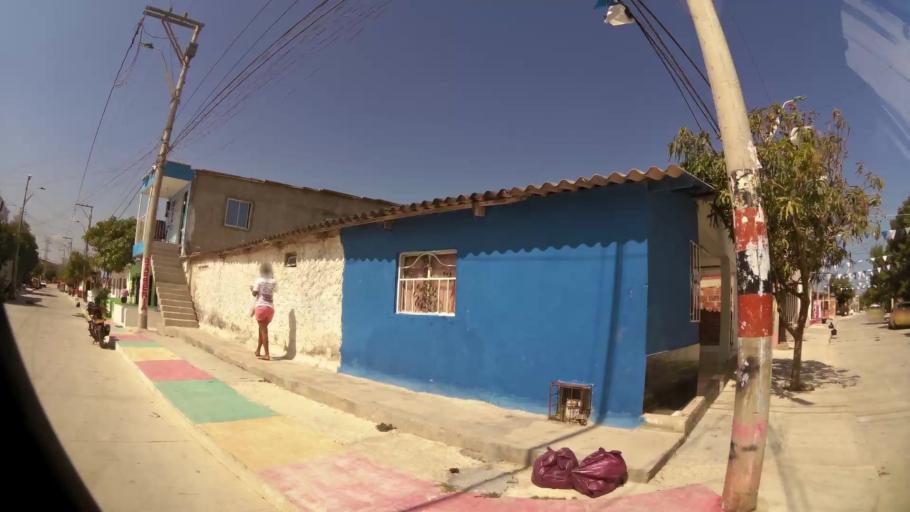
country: CO
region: Atlantico
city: Barranquilla
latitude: 10.9687
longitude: -74.8365
